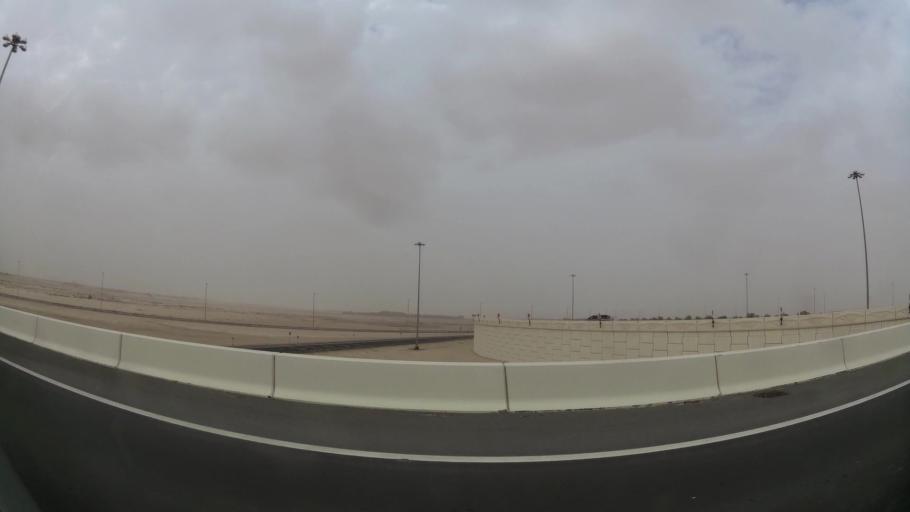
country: AE
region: Abu Dhabi
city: Abu Dhabi
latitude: 24.4123
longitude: 54.7150
